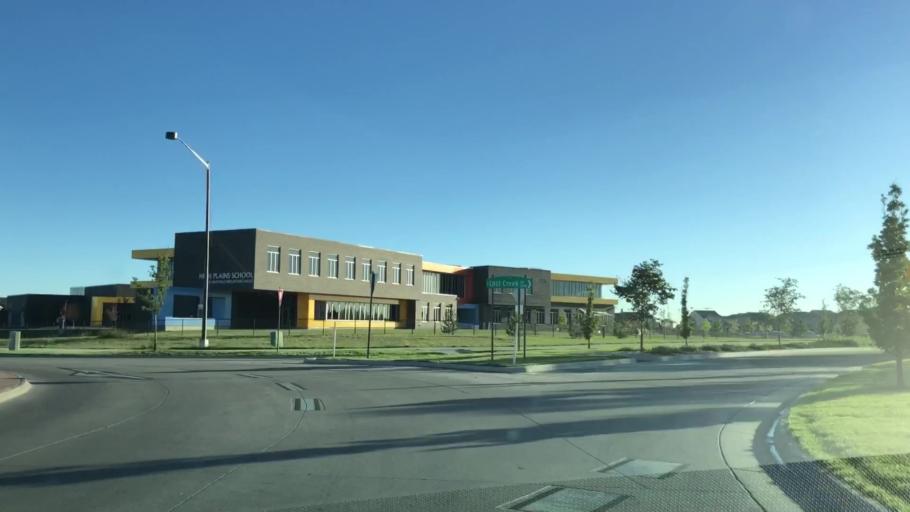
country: US
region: Colorado
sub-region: Larimer County
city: Loveland
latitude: 40.4143
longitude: -105.0209
